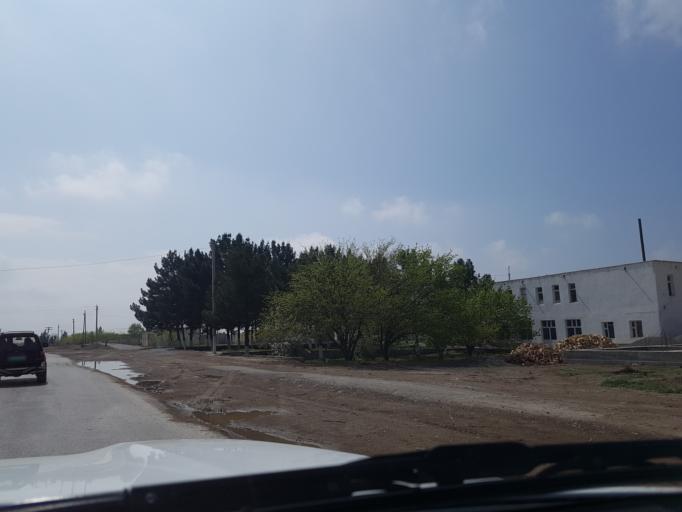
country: TM
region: Lebap
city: Turkmenabat
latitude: 38.9694
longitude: 63.6815
